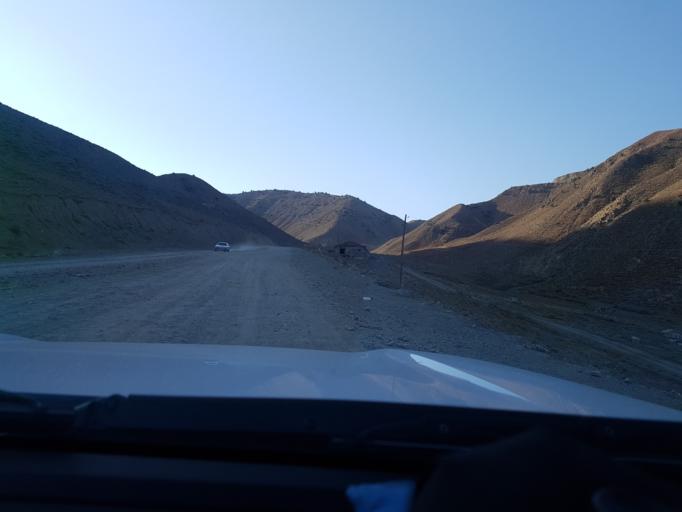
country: TM
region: Ahal
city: Baharly
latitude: 38.4518
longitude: 57.0461
